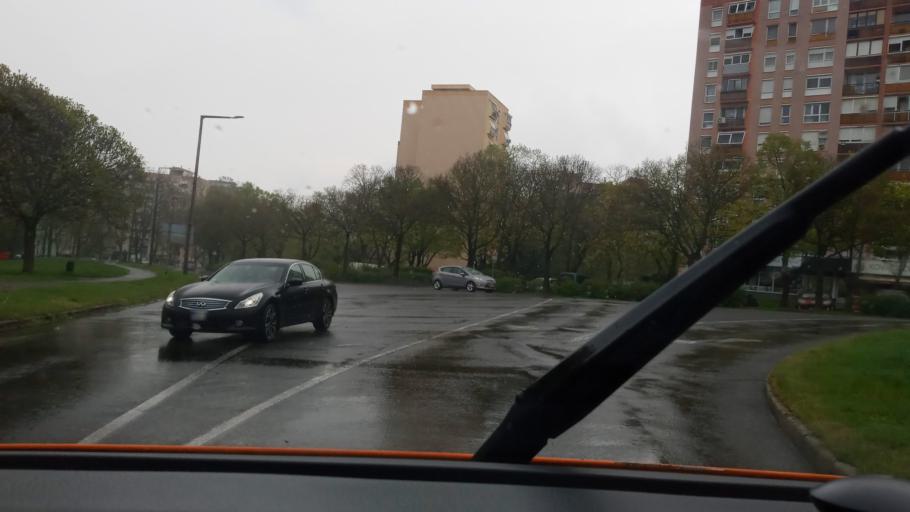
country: HU
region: Baranya
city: Pecs
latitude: 46.0384
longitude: 18.2188
